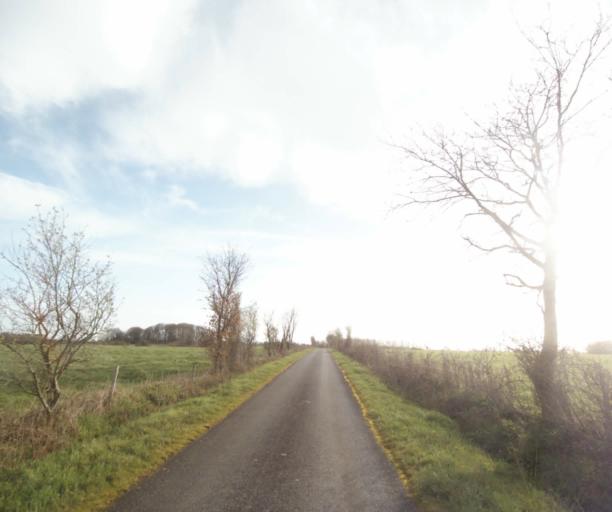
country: FR
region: Pays de la Loire
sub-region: Departement de la Loire-Atlantique
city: Bouvron
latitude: 47.3996
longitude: -1.8759
